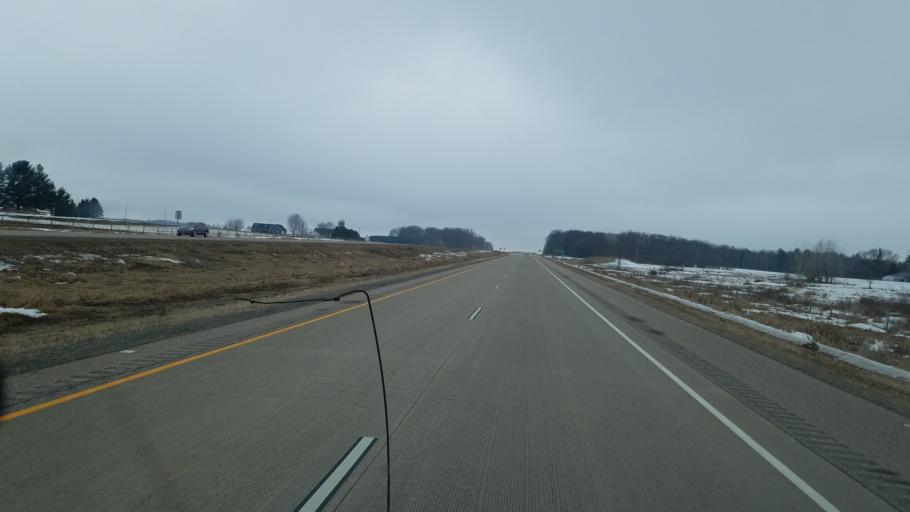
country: US
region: Wisconsin
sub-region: Wood County
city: Wisconsin Rapids
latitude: 44.6202
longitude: -89.8800
